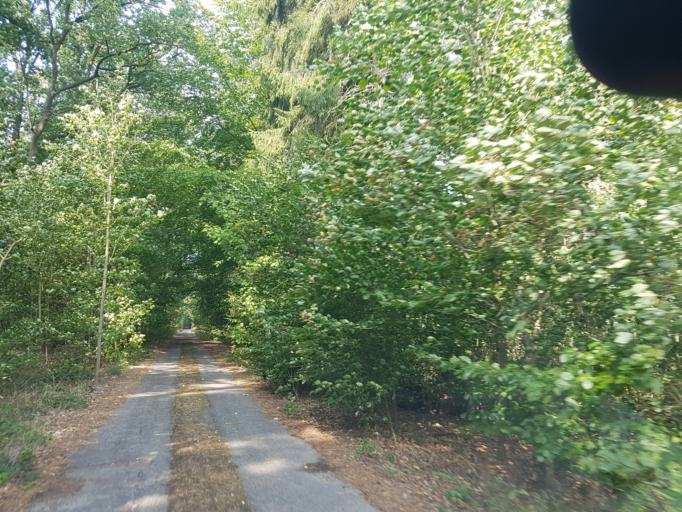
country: DE
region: Brandenburg
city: Gorzke
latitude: 52.0600
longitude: 12.2739
